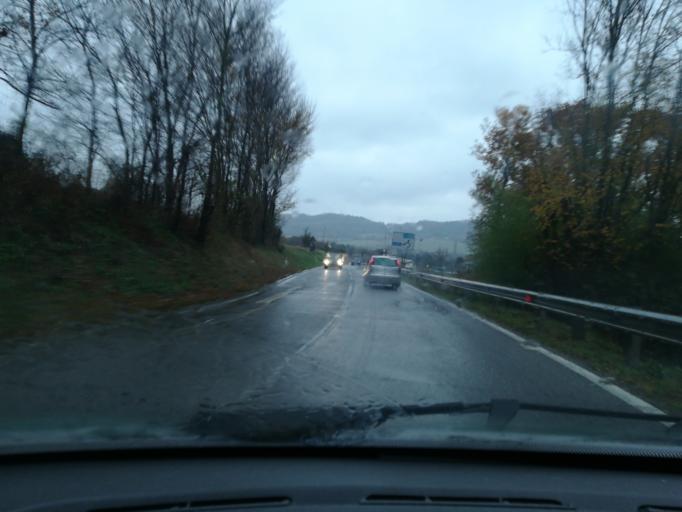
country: IT
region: The Marches
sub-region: Provincia di Macerata
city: Sforzacosta
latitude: 43.2612
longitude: 13.4219
